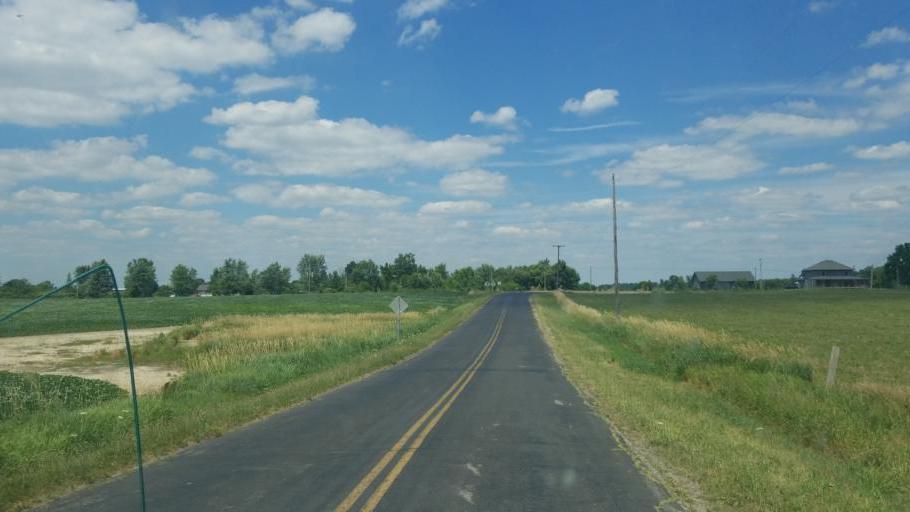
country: US
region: Ohio
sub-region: Williams County
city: Edgerton
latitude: 41.4642
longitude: -84.7104
